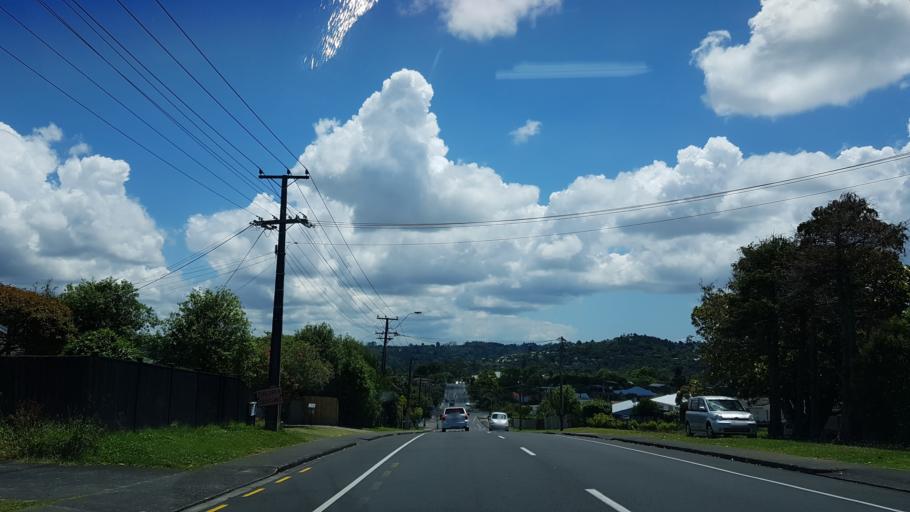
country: NZ
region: Auckland
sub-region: Auckland
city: North Shore
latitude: -36.7973
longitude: 174.7009
